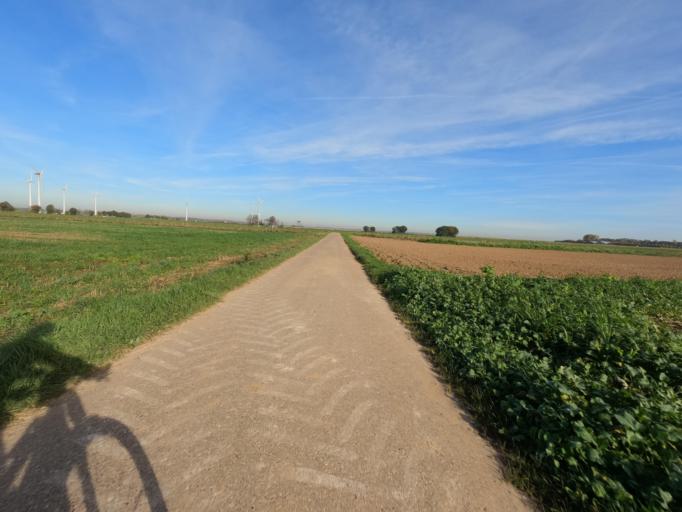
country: DE
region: North Rhine-Westphalia
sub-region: Regierungsbezirk Koln
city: Titz
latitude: 51.0550
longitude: 6.4098
